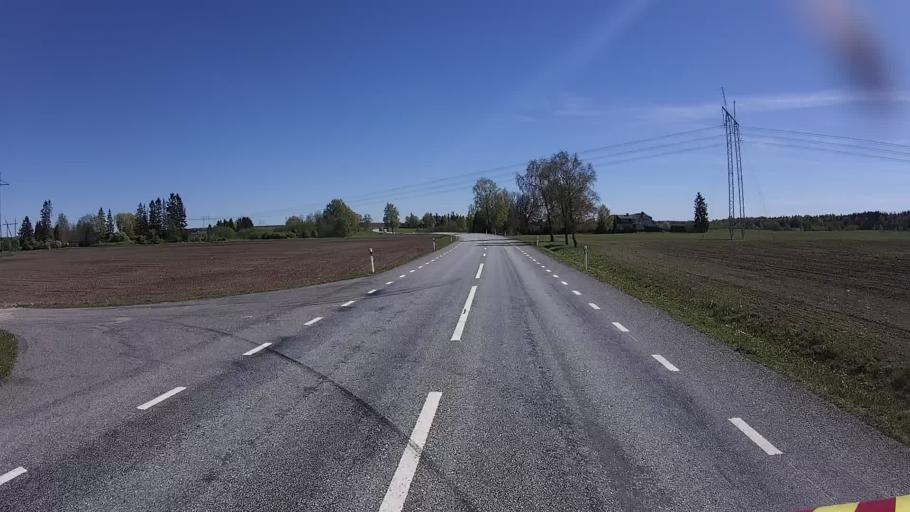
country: EE
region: Laeaene-Virumaa
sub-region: Tapa vald
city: Tapa
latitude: 59.2352
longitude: 25.7049
